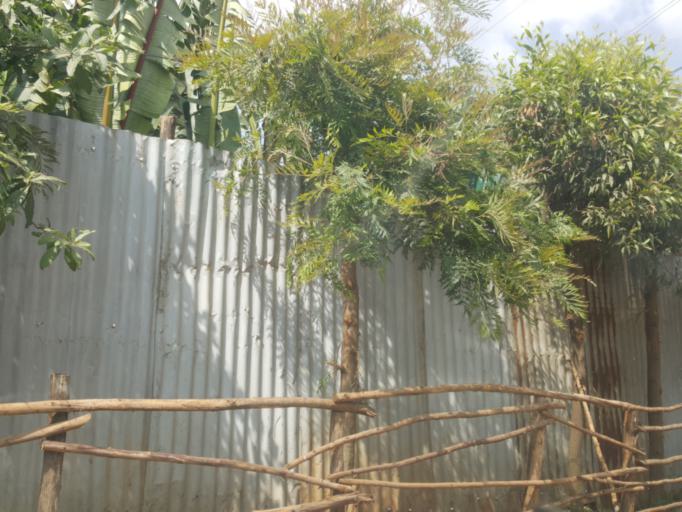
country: ET
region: Adis Abeba
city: Addis Ababa
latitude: 9.0580
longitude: 38.7207
